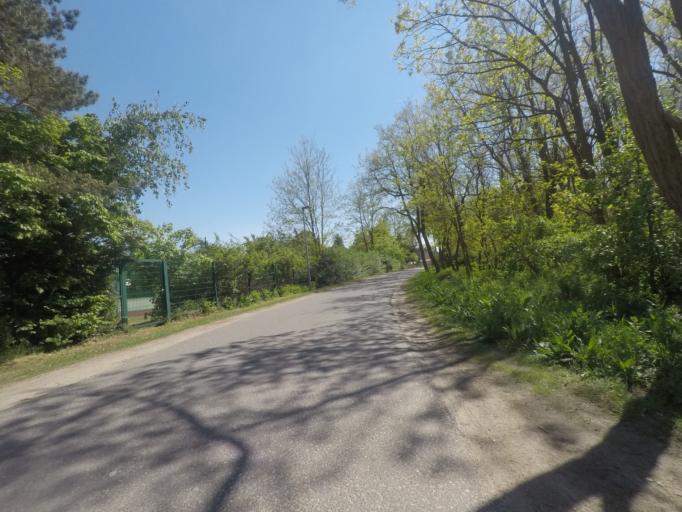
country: DE
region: Brandenburg
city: Melchow
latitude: 52.8403
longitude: 13.6827
